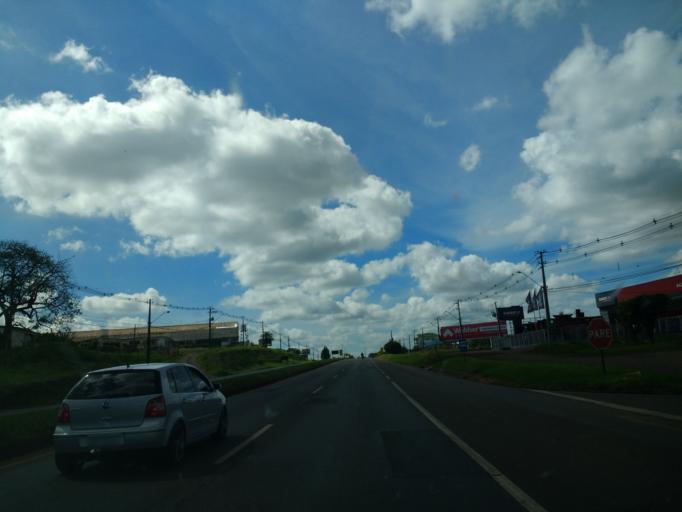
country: BR
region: Parana
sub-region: Maringa
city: Maringa
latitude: -23.4409
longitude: -51.9802
